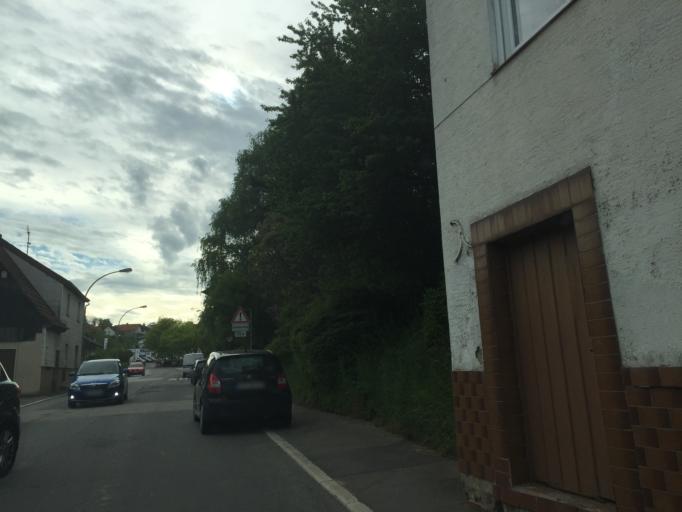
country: DE
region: Baden-Wuerttemberg
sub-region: Karlsruhe Region
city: Wilhelmsfeld
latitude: 49.5107
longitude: 8.7281
